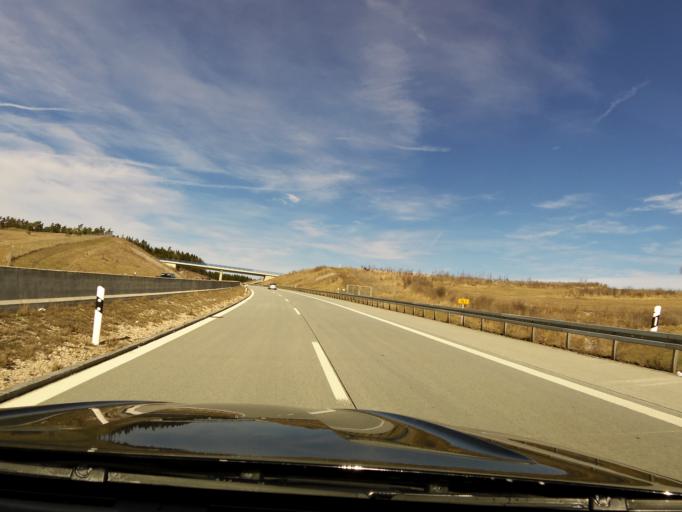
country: DE
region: Bavaria
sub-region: Upper Palatinate
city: Schierling
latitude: 48.7778
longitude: 12.1438
